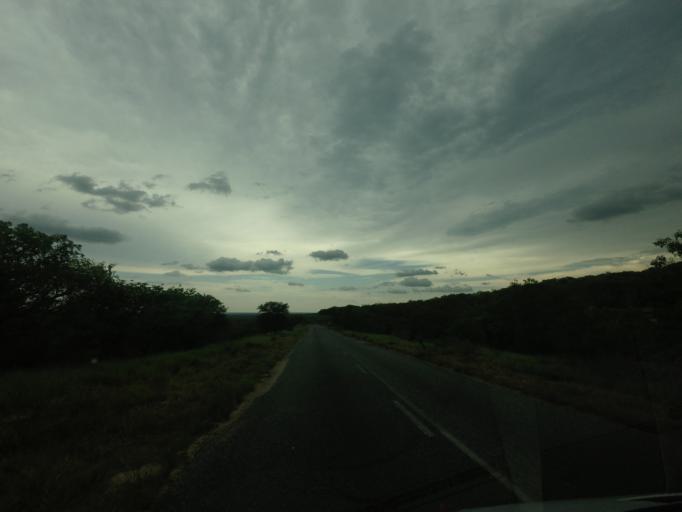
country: ZA
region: Limpopo
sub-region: Mopani District Municipality
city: Hoedspruit
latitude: -24.5069
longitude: 30.9050
